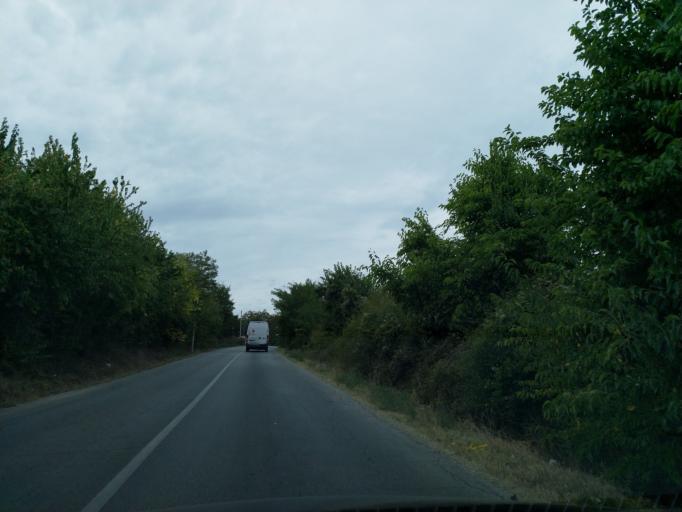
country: RS
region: Central Serbia
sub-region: Pomoravski Okrug
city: Jagodina
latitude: 43.9916
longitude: 21.2287
